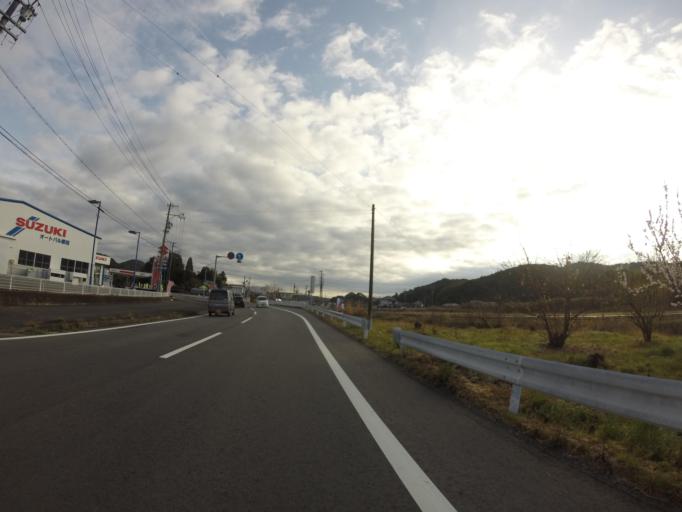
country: JP
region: Shizuoka
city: Hamakita
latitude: 34.8217
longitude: 137.7135
